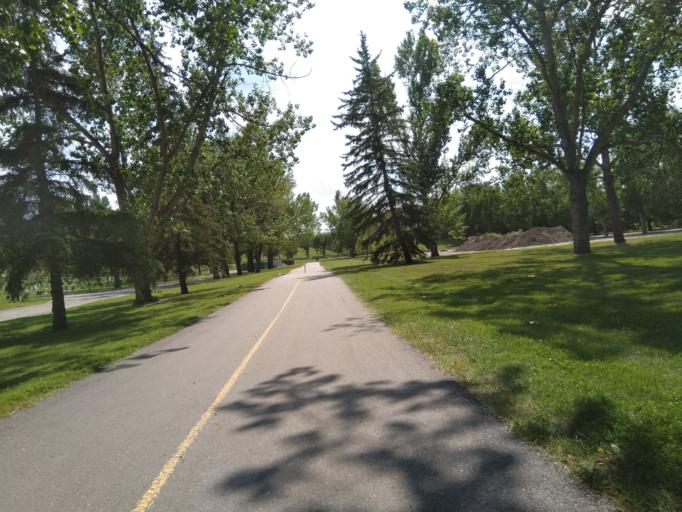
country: CA
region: Alberta
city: Calgary
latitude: 51.0835
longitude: -114.0748
